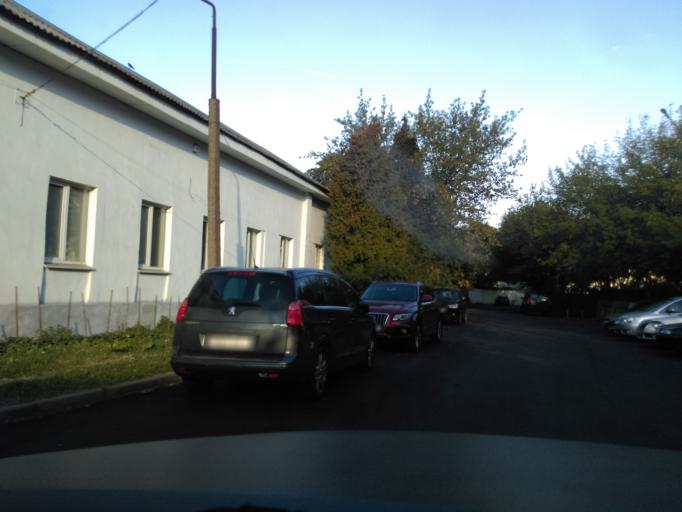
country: BY
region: Minsk
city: Minsk
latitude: 53.9131
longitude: 27.5928
